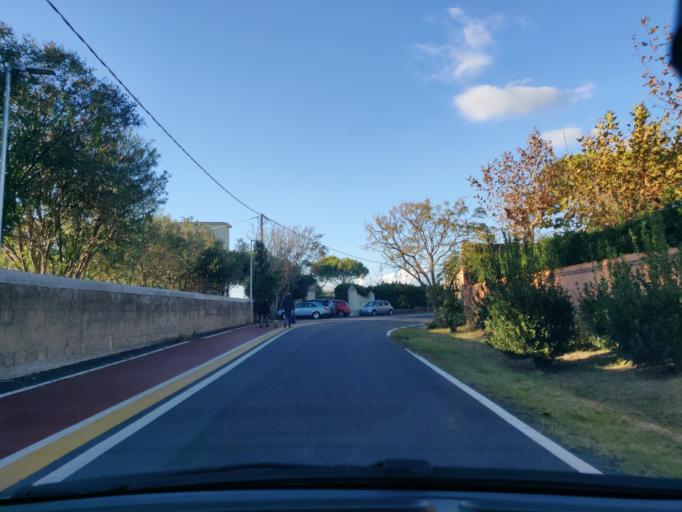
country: IT
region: Latium
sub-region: Provincia di Viterbo
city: Tarquinia
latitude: 42.2128
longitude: 11.7087
